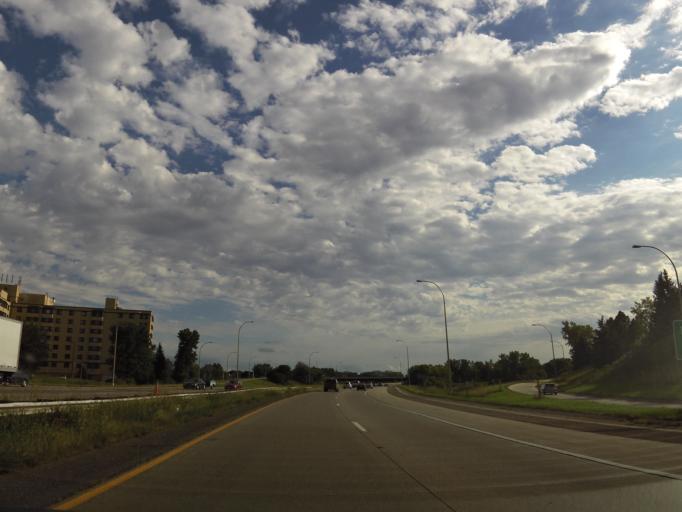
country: US
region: Minnesota
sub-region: Hennepin County
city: Minnetonka Mills
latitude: 44.9384
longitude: -93.3966
